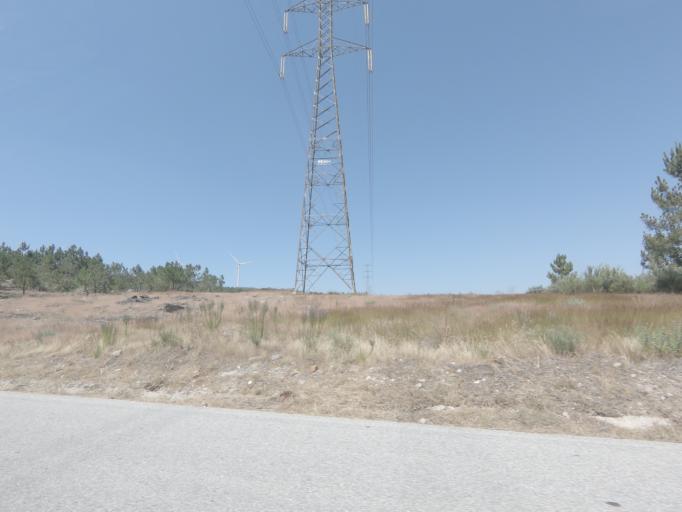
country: PT
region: Viseu
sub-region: Tarouca
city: Tarouca
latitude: 40.9826
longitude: -7.7904
